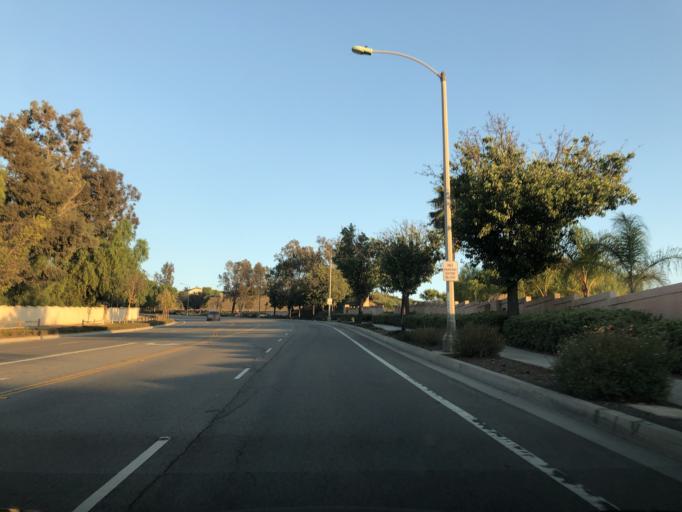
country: US
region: California
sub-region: Riverside County
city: Corona
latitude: 33.8979
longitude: -117.5529
